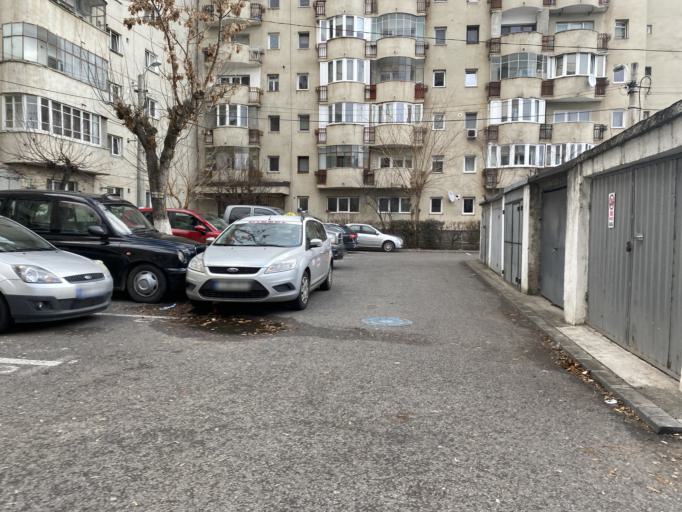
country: RO
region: Cluj
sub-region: Municipiul Cluj-Napoca
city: Cluj-Napoca
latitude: 46.7601
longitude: 23.5636
